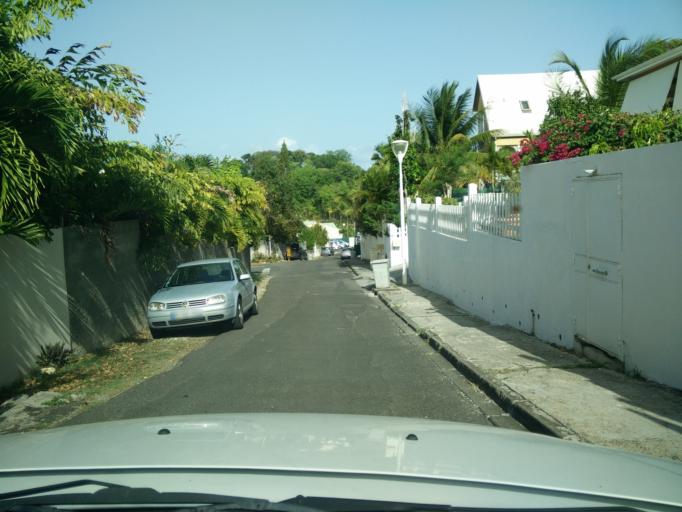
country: GP
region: Guadeloupe
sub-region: Guadeloupe
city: Le Gosier
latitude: 16.2006
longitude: -61.4714
